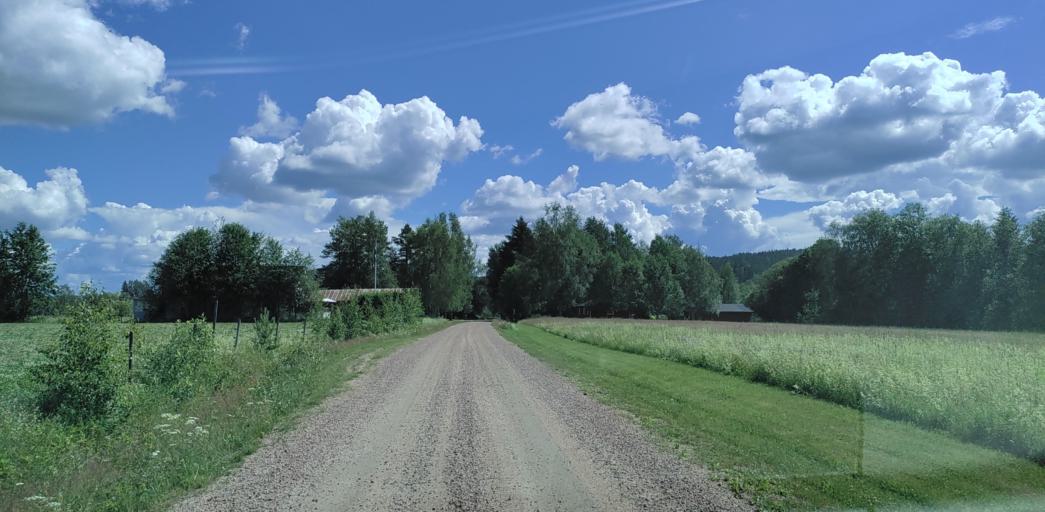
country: SE
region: Vaermland
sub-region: Munkfors Kommun
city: Munkfors
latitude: 59.9518
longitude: 13.4936
